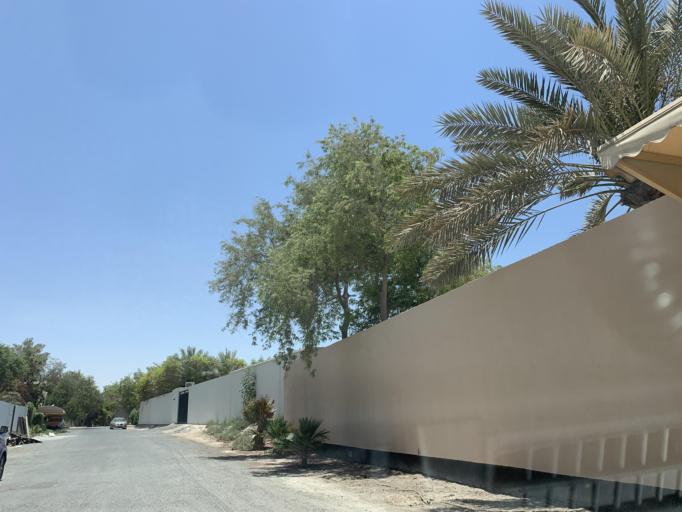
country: BH
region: Manama
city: Jidd Hafs
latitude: 26.2274
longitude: 50.4868
